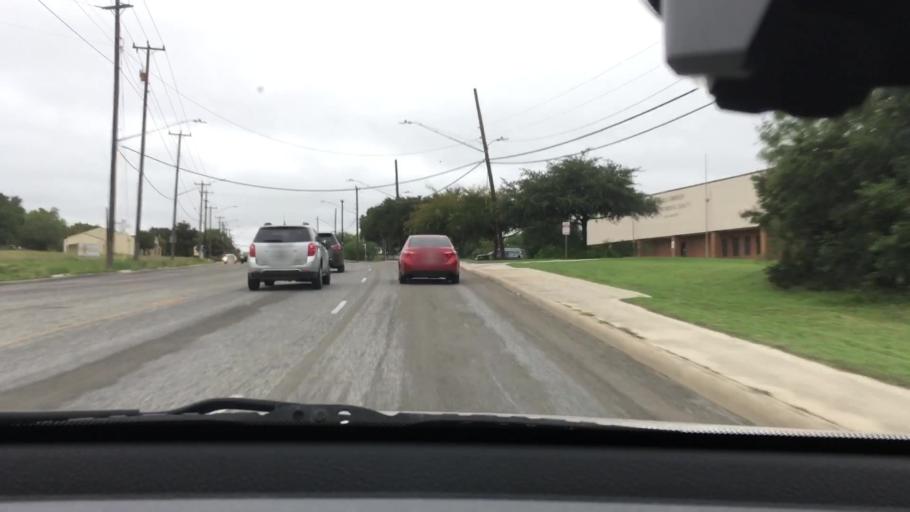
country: US
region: Texas
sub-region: Bexar County
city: Live Oak
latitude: 29.5700
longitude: -98.3672
